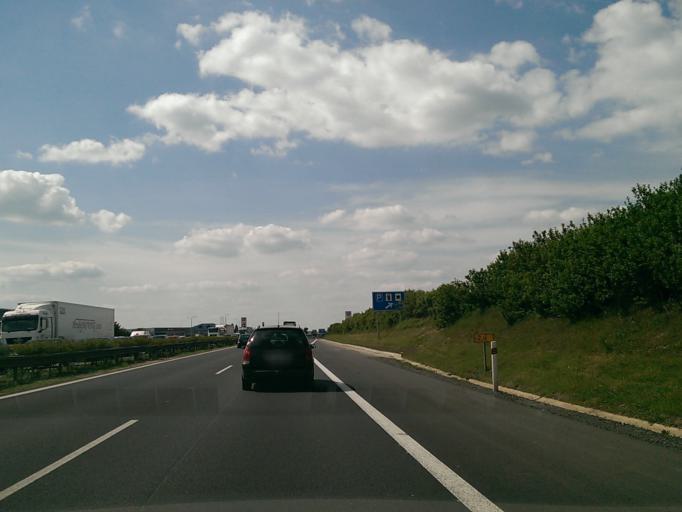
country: CZ
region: Central Bohemia
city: Zdiby
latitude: 50.1677
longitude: 14.4645
